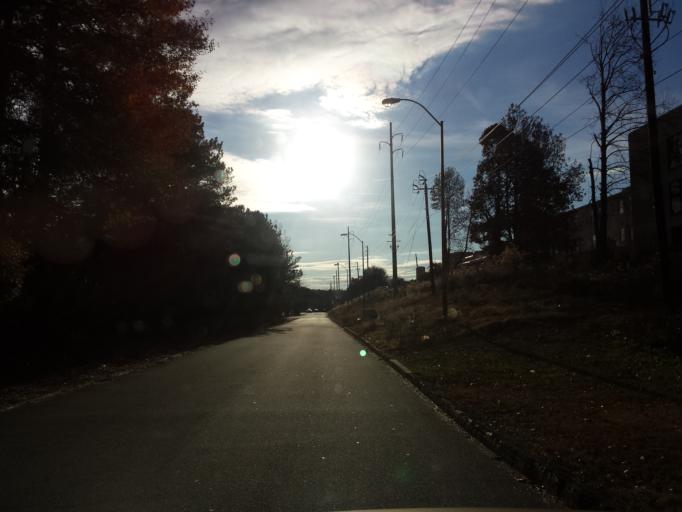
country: US
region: Georgia
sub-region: Cobb County
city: Vinings
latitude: 33.9001
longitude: -84.4777
